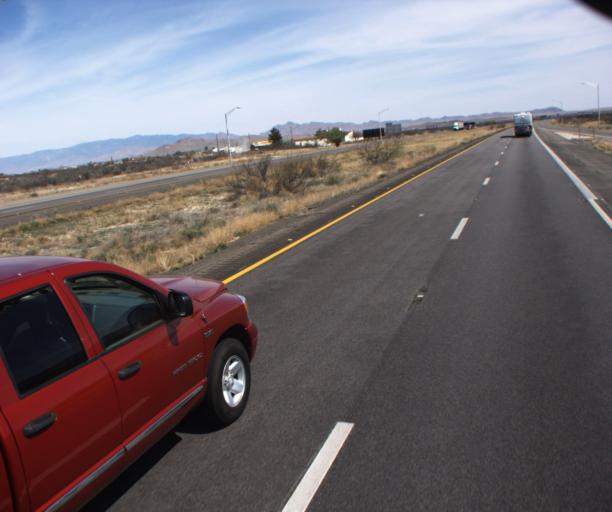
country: US
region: Arizona
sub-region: Cochise County
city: Willcox
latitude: 32.2688
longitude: -109.8418
